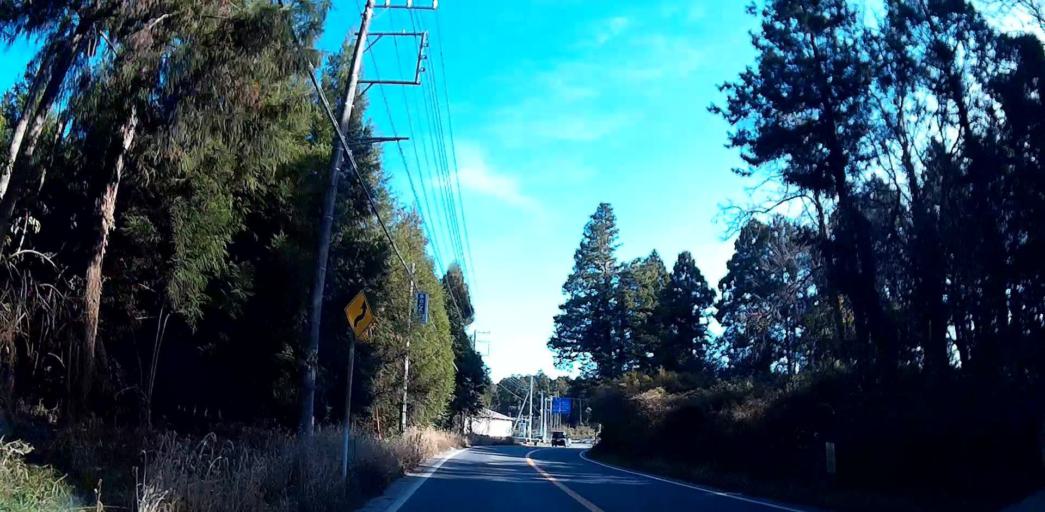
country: JP
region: Chiba
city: Yokaichiba
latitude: 35.7593
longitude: 140.4544
